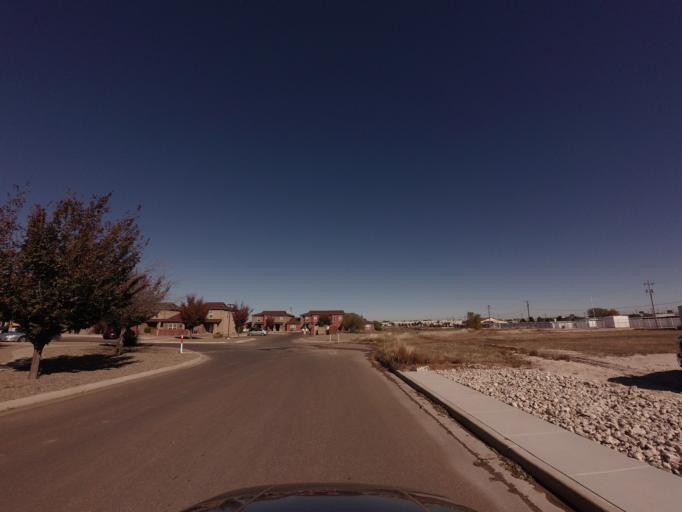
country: US
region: New Mexico
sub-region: Curry County
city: Clovis
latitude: 34.4316
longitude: -103.2026
